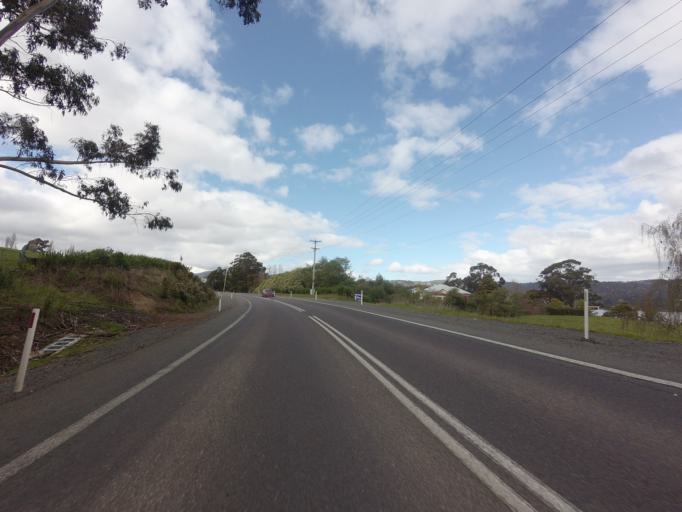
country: AU
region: Tasmania
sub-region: Huon Valley
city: Franklin
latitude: -43.1306
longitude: 146.9877
